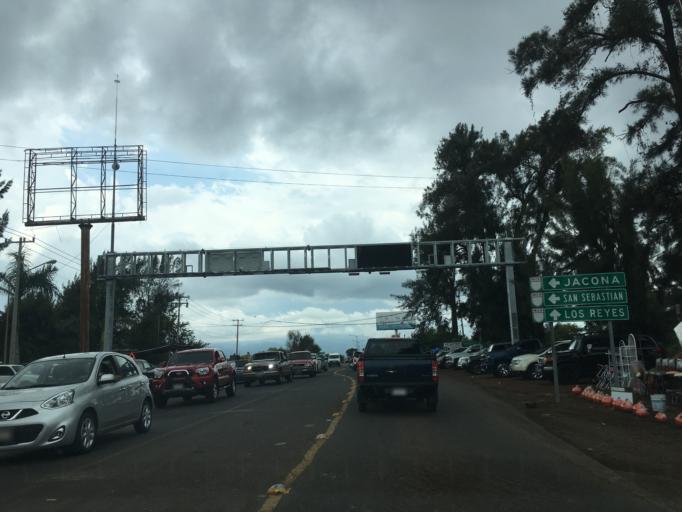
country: MX
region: Michoacan
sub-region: Periban
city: Gildardo Magana (Los Angeles)
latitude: 19.5758
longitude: -102.4602
